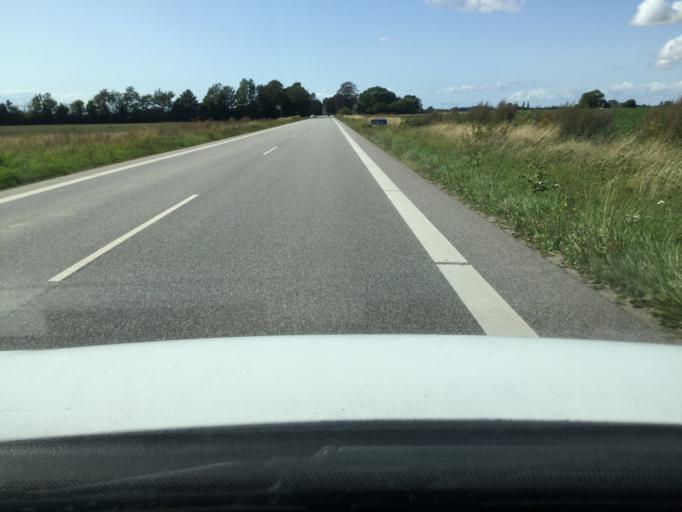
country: DK
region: Zealand
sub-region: Lolland Kommune
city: Rodby
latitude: 54.7563
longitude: 11.3492
